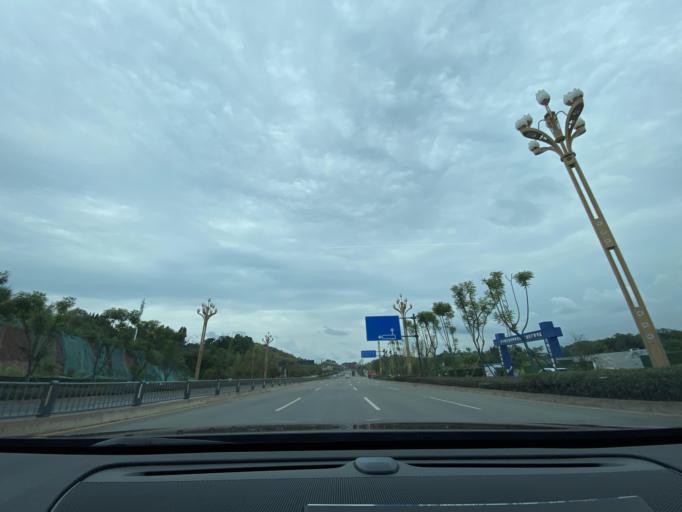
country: CN
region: Sichuan
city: Jiancheng
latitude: 30.4803
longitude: 104.4854
